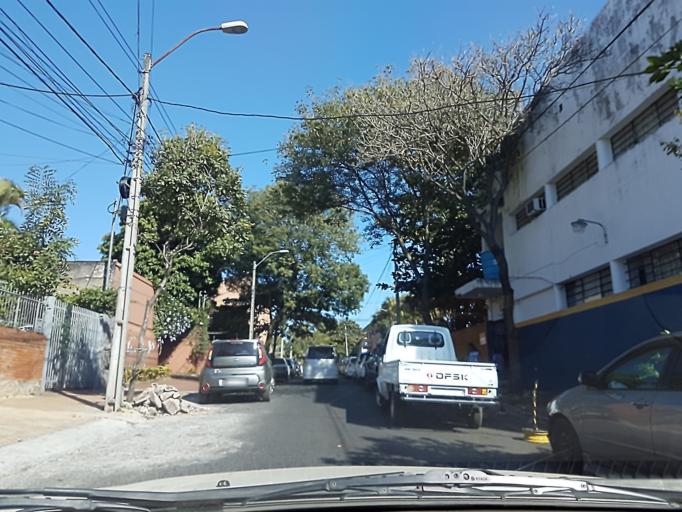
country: PY
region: Asuncion
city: Asuncion
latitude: -25.2849
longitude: -57.6025
